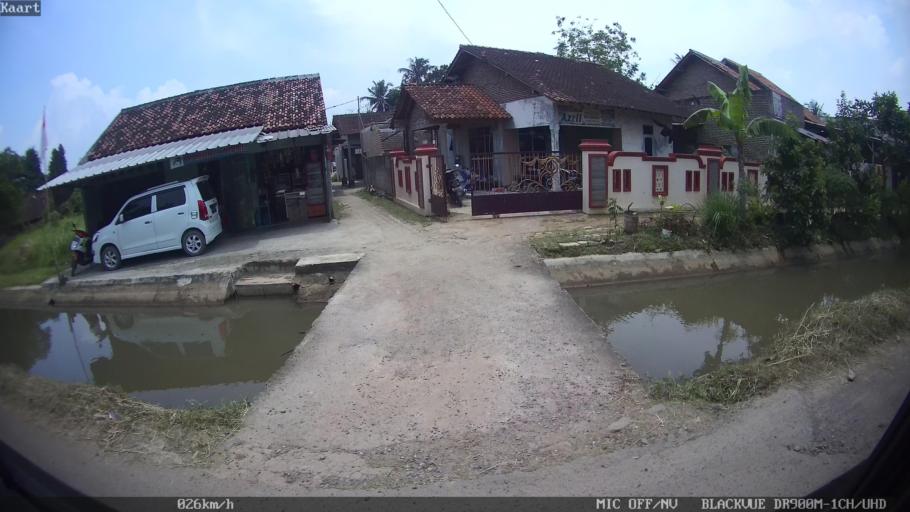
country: ID
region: Lampung
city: Kedaton
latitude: -5.3417
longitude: 105.2465
